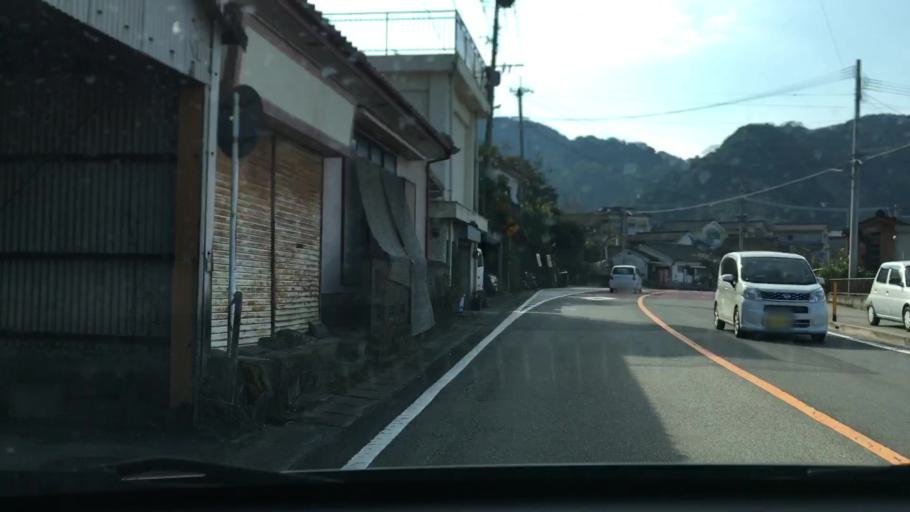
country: JP
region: Kagoshima
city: Hamanoichi
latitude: 31.6126
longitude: 130.7964
